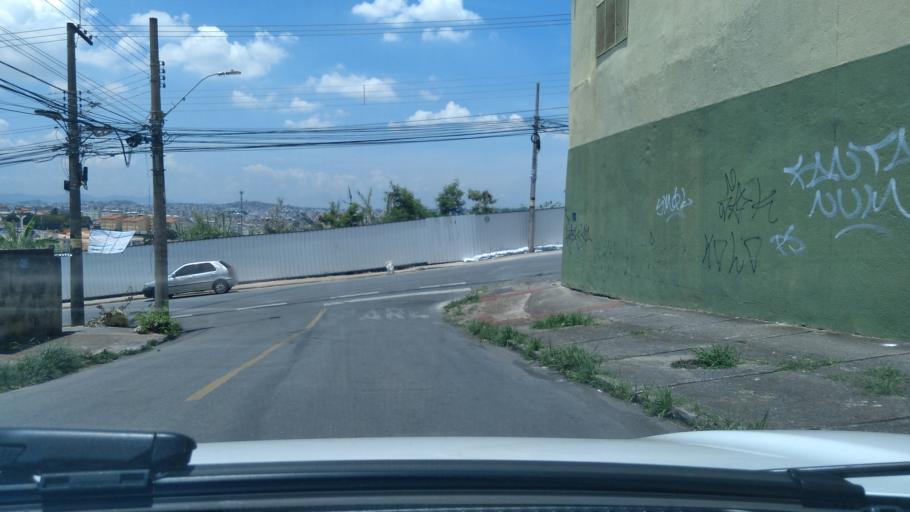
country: BR
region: Minas Gerais
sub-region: Contagem
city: Contagem
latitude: -19.9276
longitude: -44.0140
